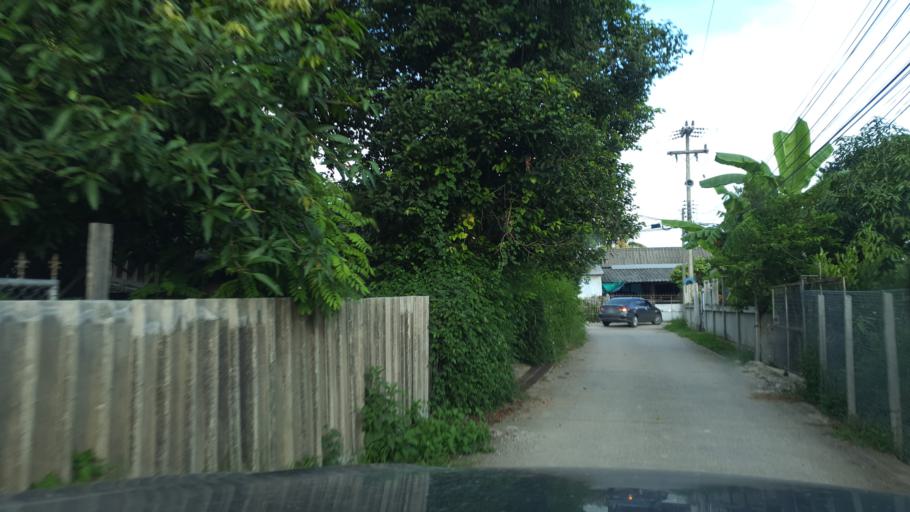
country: TH
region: Lamphun
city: Ban Thi
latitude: 18.6508
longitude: 99.1072
